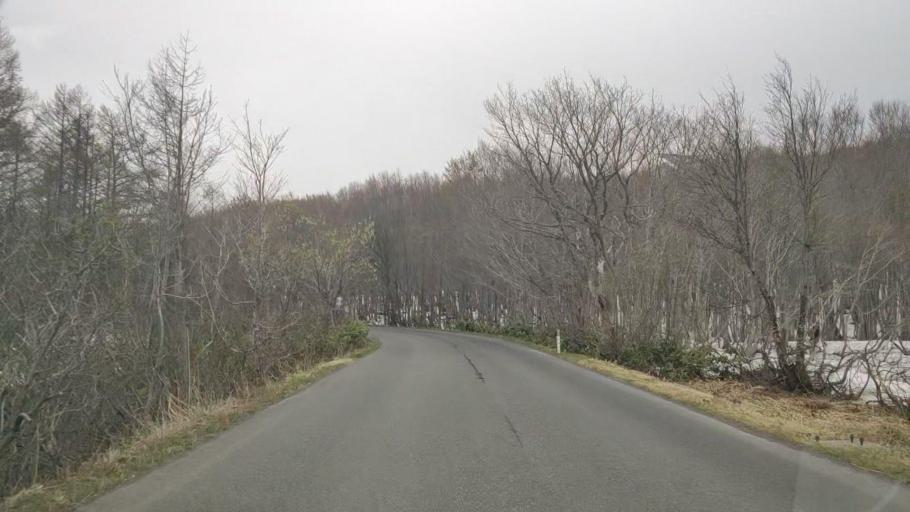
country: JP
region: Aomori
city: Aomori Shi
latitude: 40.6845
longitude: 140.9263
